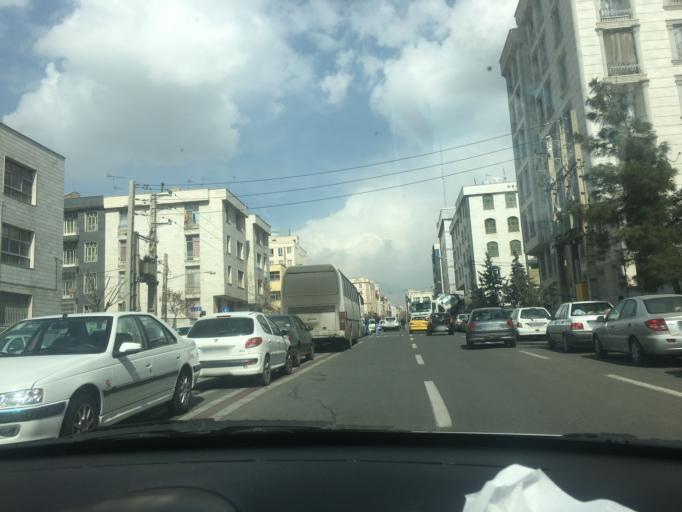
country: IR
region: Tehran
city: Tehran
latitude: 35.7215
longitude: 51.3178
